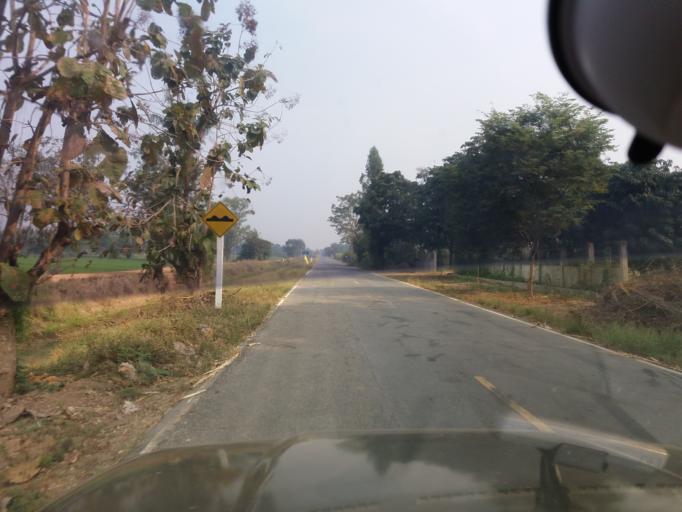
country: TH
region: Suphan Buri
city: Doem Bang Nang Buat
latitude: 14.8644
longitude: 100.1686
